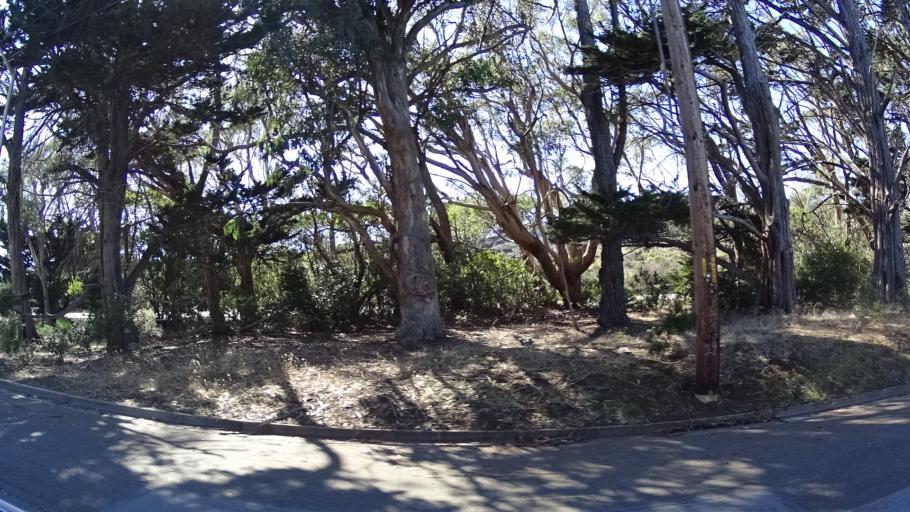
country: US
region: California
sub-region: San Mateo County
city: San Bruno
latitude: 37.6164
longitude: -122.4395
